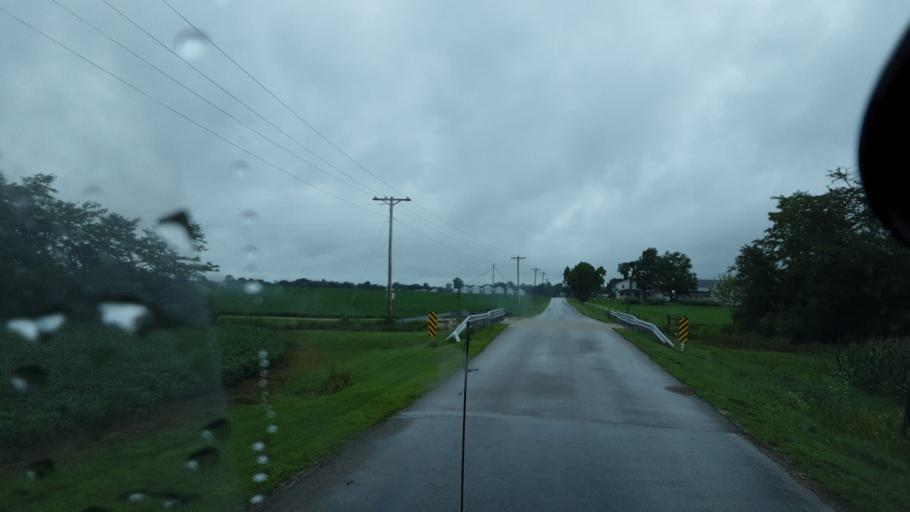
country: US
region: Indiana
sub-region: Adams County
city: Decatur
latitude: 40.7675
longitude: -84.8607
